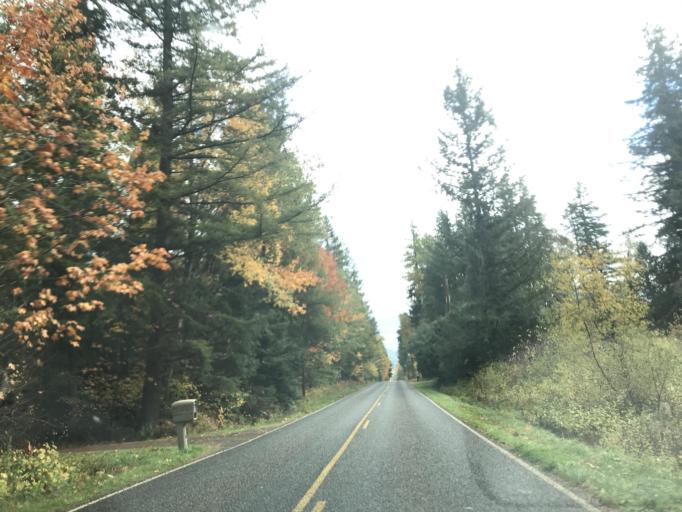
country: US
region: Washington
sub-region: Whatcom County
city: Geneva
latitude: 48.8184
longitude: -122.3694
